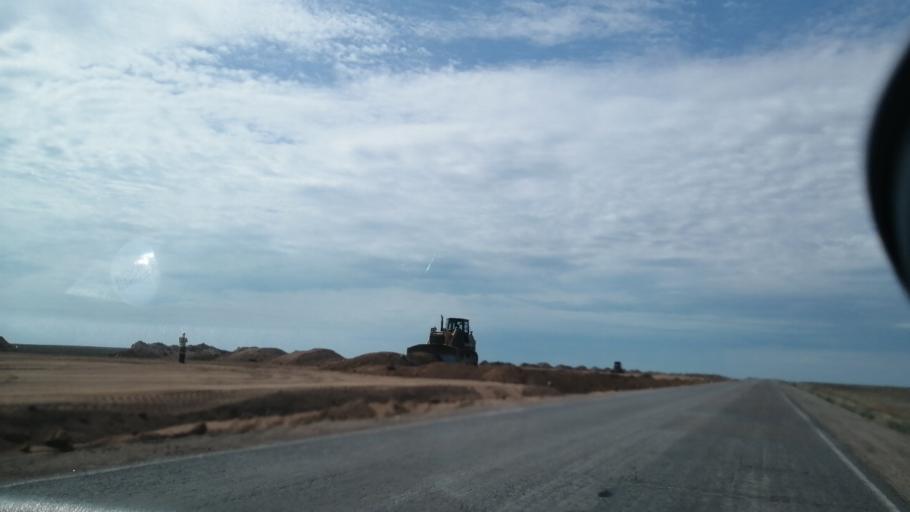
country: KZ
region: Qaraghandy
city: Balqash
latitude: 46.7055
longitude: 74.4517
